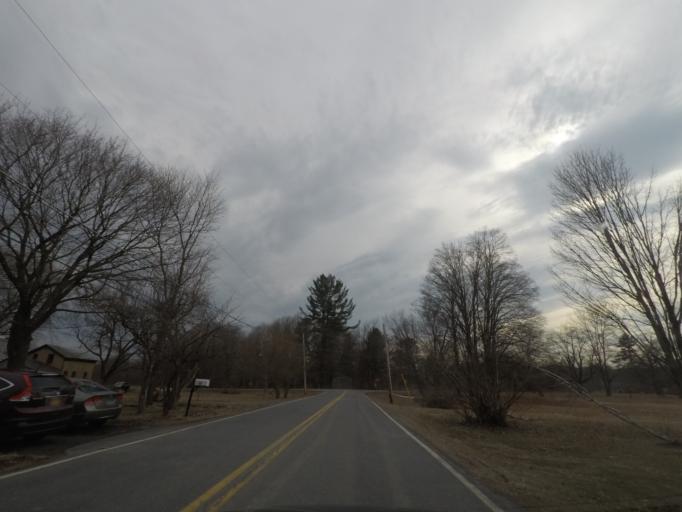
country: US
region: New York
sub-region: Saratoga County
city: Schuylerville
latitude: 43.1184
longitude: -73.5730
